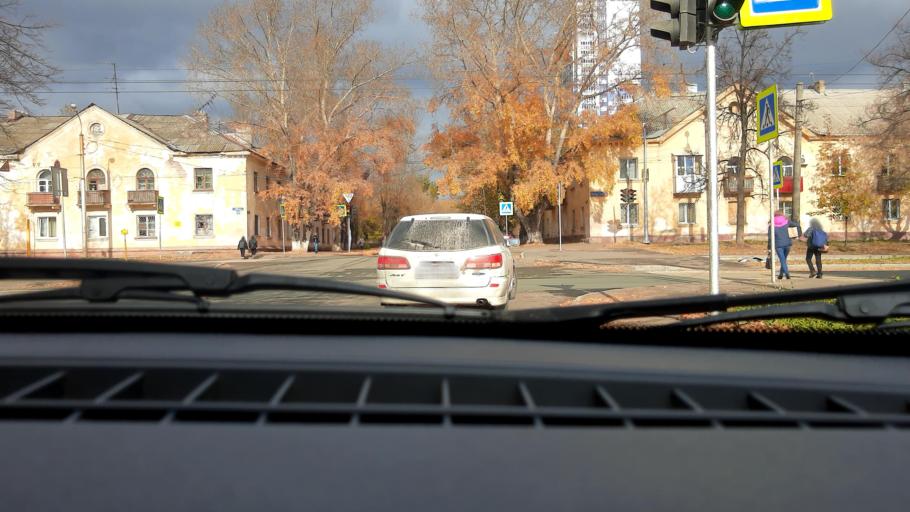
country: RU
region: Bashkortostan
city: Ufa
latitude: 54.8129
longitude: 56.1094
